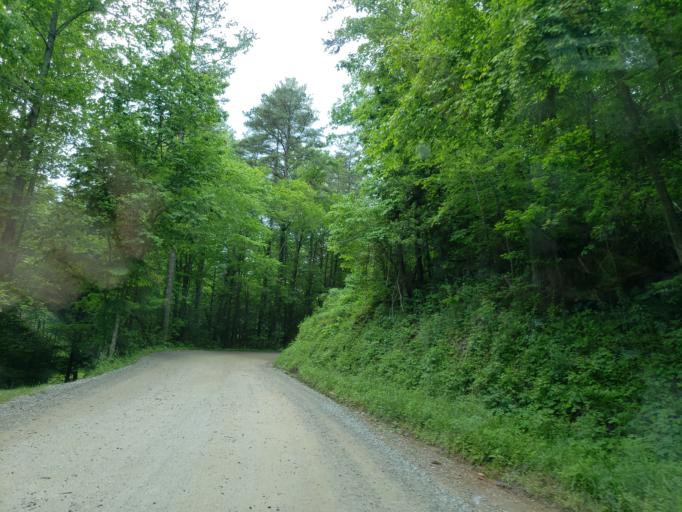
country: US
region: Georgia
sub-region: Fannin County
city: Blue Ridge
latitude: 34.8533
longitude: -84.4190
